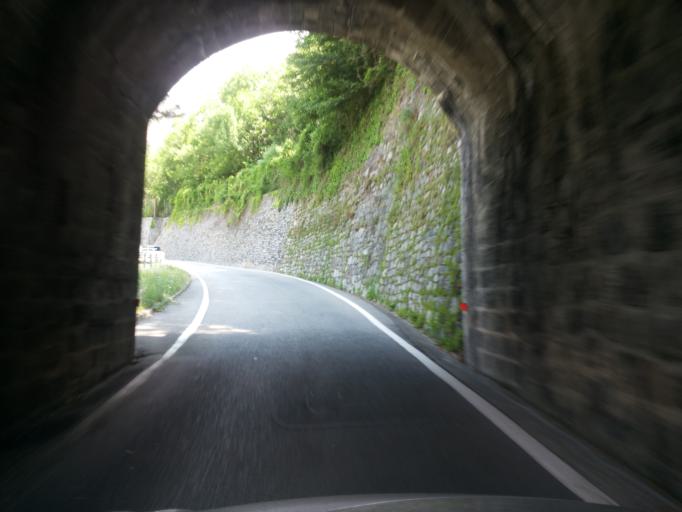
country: IT
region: Aosta Valley
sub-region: Valle d'Aosta
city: Pont-Saint-Martin
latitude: 45.5995
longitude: 7.8047
